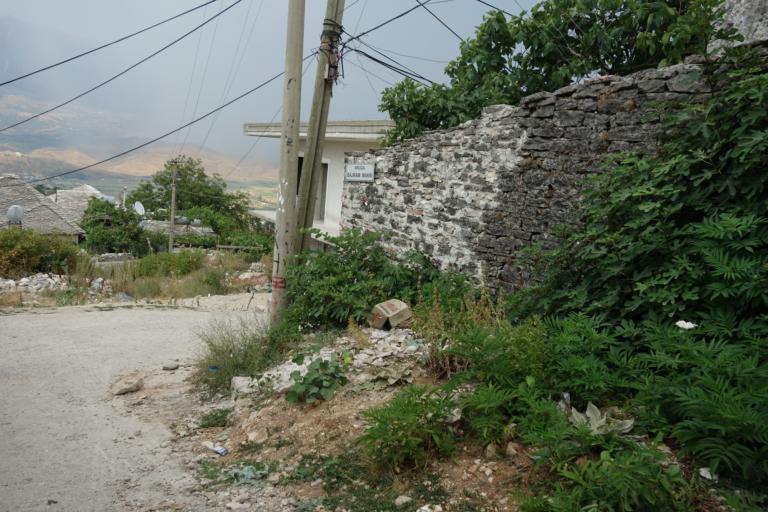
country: AL
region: Gjirokaster
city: Gjirokaster
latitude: 40.0680
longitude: 20.1368
